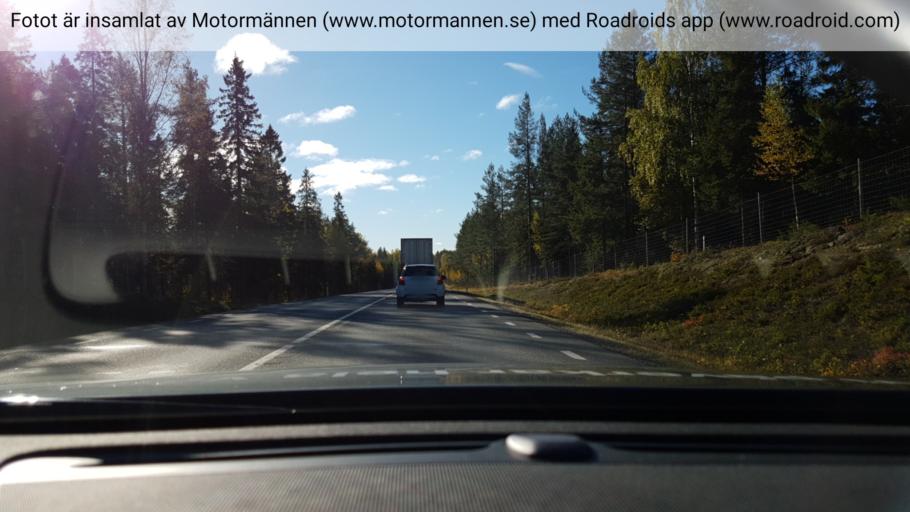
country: SE
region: Vaesterbotten
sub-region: Skelleftea Kommun
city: Burea
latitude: 64.5344
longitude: 21.2587
